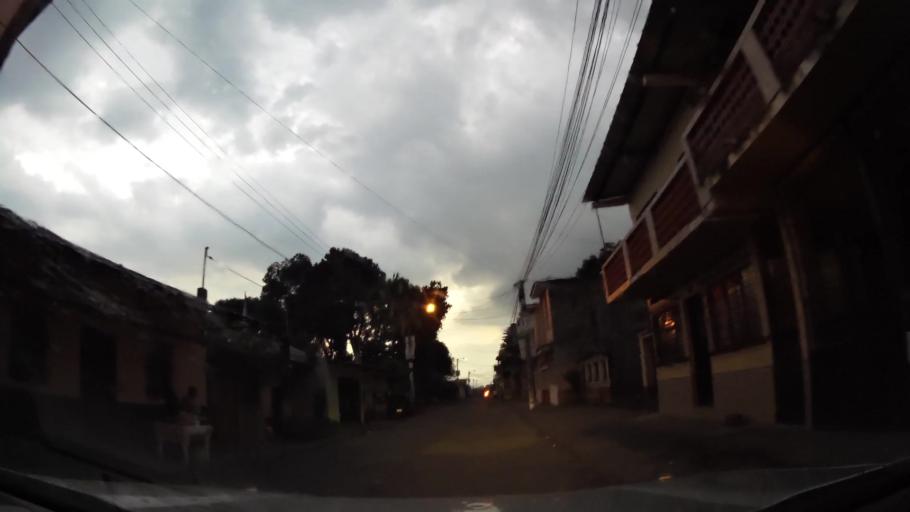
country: GT
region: Escuintla
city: Santa Lucia Cotzumalguapa
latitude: 14.3408
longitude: -91.0250
